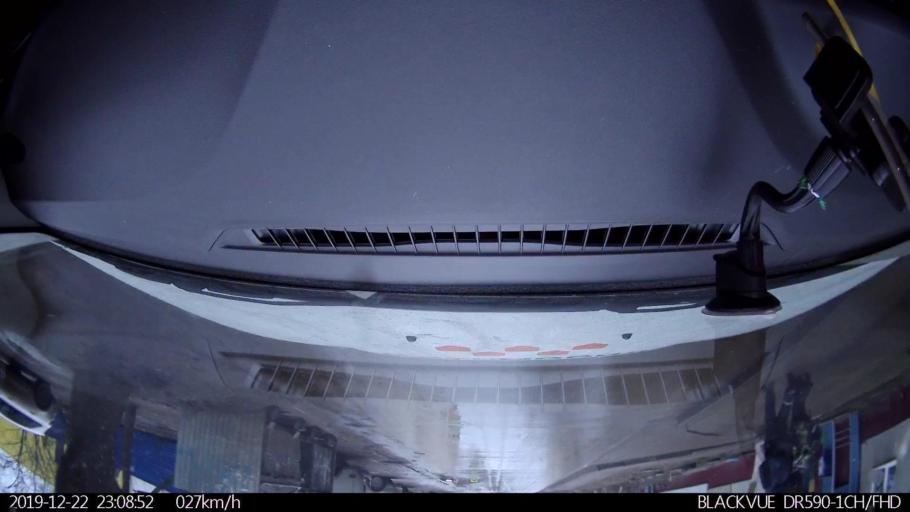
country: RU
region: Nizjnij Novgorod
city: Gorbatovka
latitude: 56.2616
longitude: 43.8523
